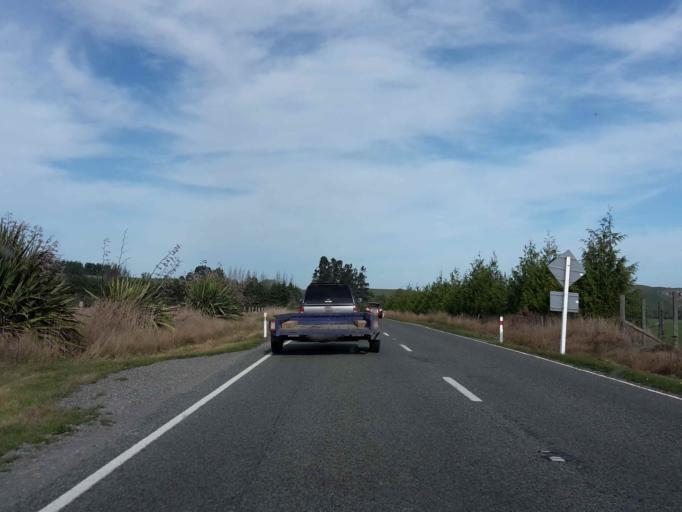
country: NZ
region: Canterbury
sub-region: Timaru District
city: Pleasant Point
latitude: -44.0864
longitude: 170.9861
